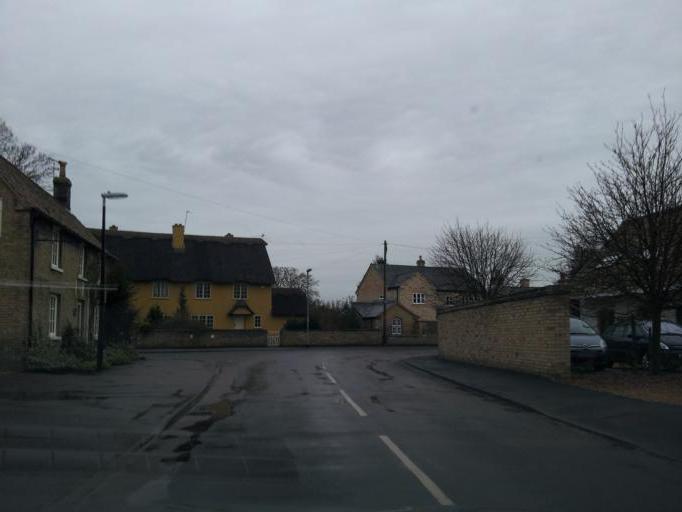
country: GB
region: England
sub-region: Cambridgeshire
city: Bottisham
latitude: 52.2405
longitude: 0.2458
